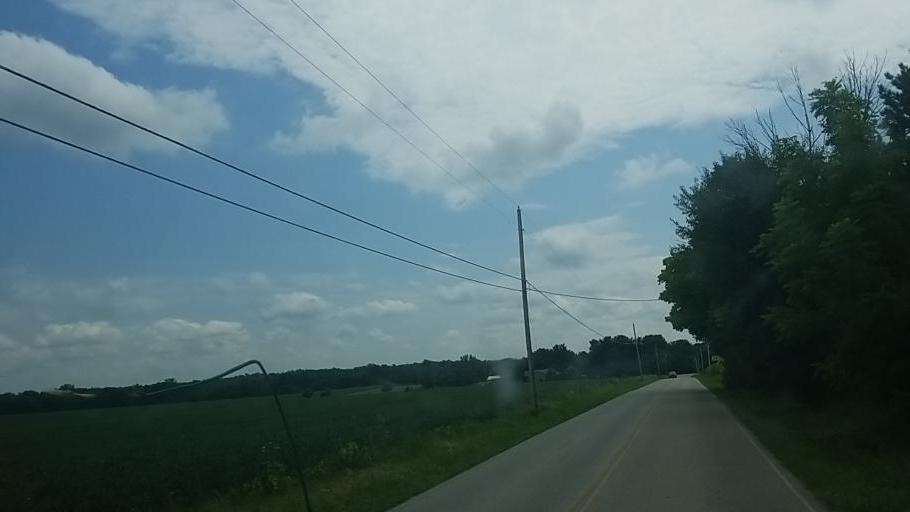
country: US
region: Ohio
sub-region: Pickaway County
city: Ashville
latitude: 39.7360
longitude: -82.8879
